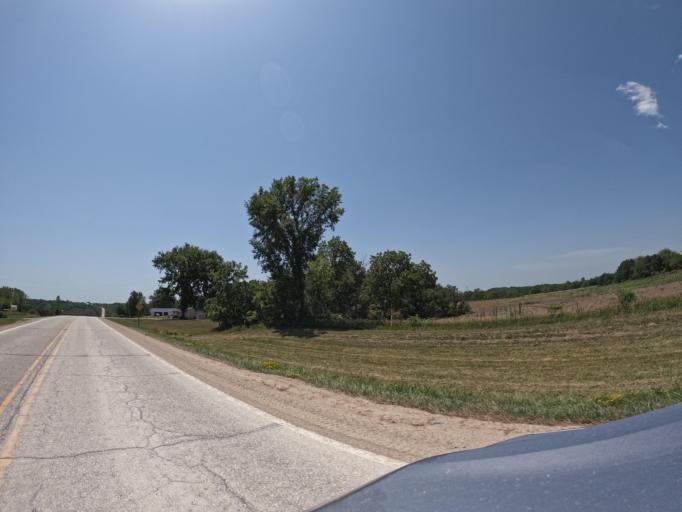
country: US
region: Iowa
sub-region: Henry County
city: Mount Pleasant
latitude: 40.9436
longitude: -91.6142
